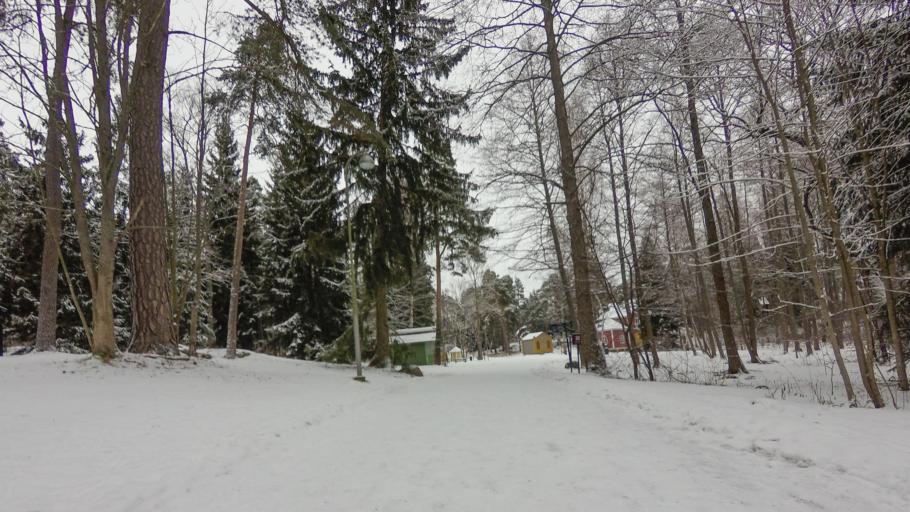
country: FI
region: Uusimaa
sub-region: Helsinki
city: Teekkarikylae
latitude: 60.1804
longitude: 24.8854
